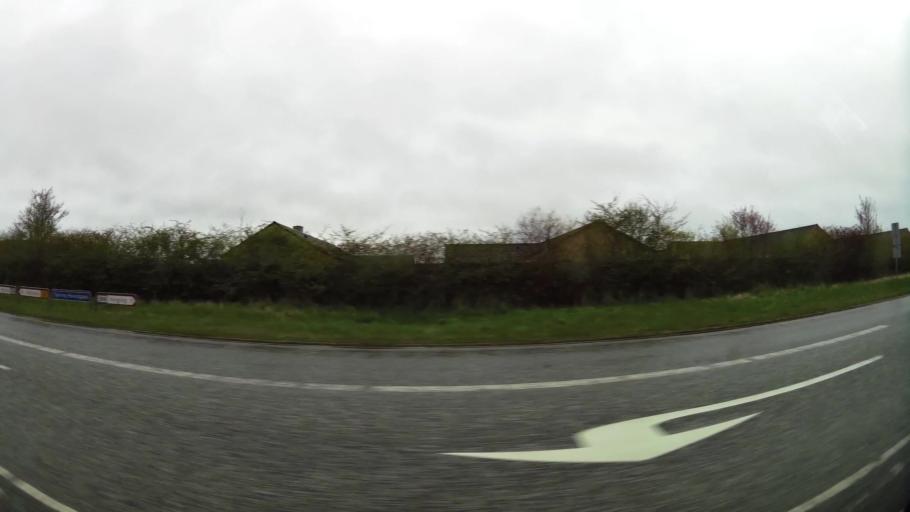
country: DK
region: Central Jutland
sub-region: Herning Kommune
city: Snejbjerg
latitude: 56.1681
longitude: 8.9182
